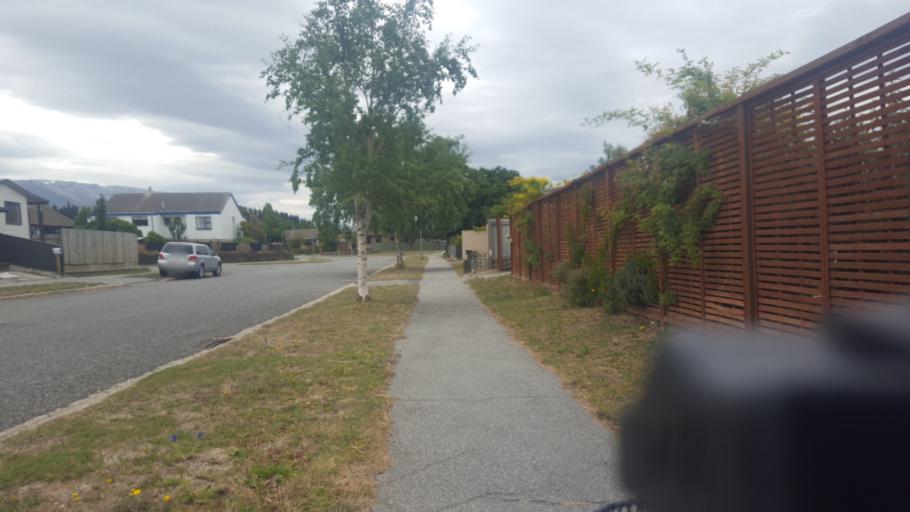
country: NZ
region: Otago
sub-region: Queenstown-Lakes District
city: Wanaka
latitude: -45.0455
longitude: 169.1849
